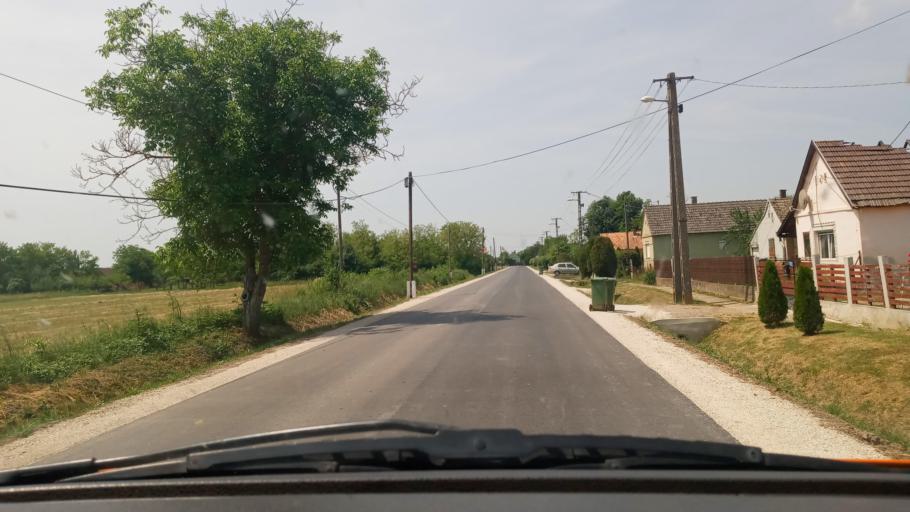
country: HU
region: Baranya
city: Szigetvar
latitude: 45.9654
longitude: 17.6611
